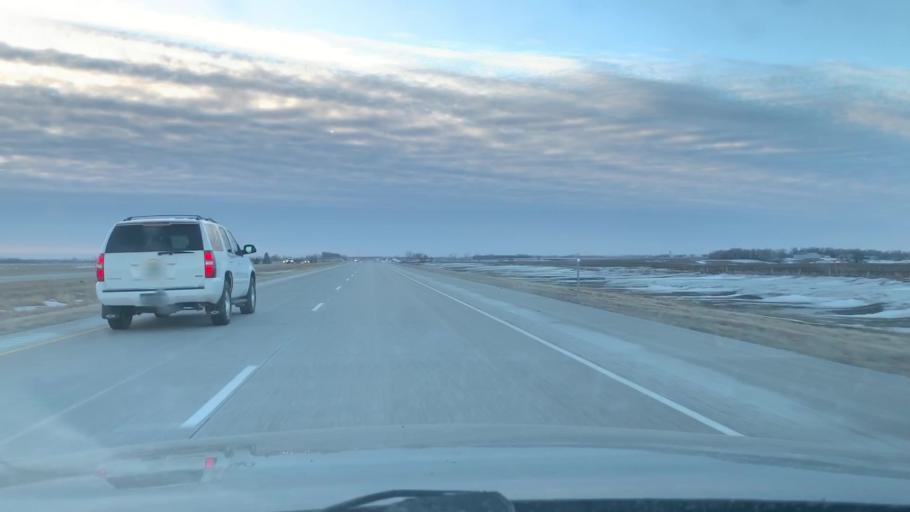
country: US
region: North Dakota
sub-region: Ransom County
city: Sheldon
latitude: 46.8762
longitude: -97.5797
